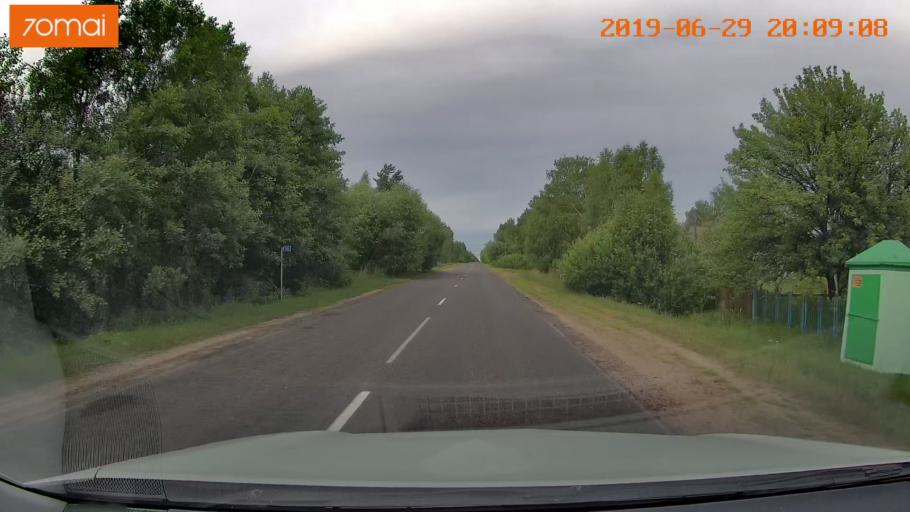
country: BY
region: Brest
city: Lahishyn
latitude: 52.3473
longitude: 26.0677
